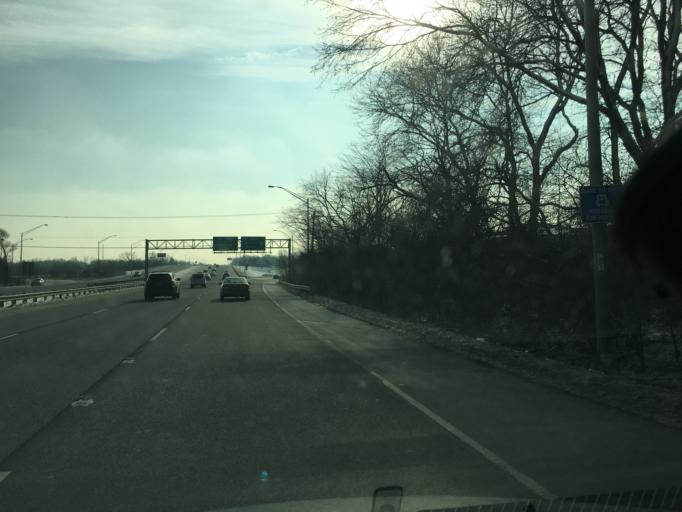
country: US
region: Illinois
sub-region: DuPage County
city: Willowbrook
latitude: 41.7460
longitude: -87.9447
